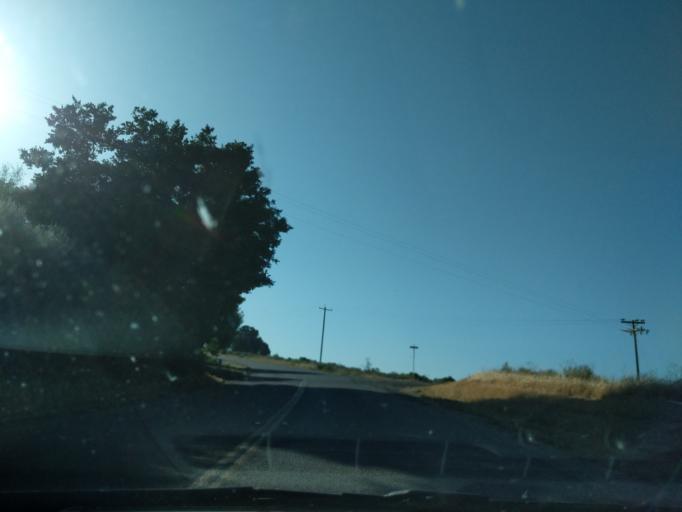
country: US
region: California
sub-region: Monterey County
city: Soledad
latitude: 36.4268
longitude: -121.4025
